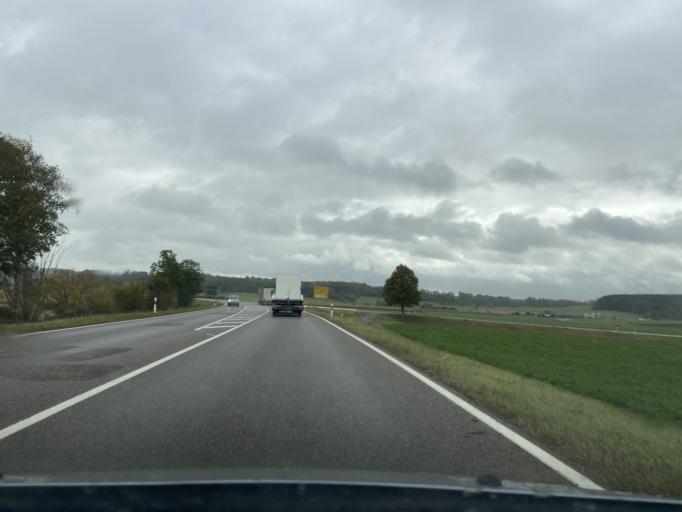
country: DE
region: Baden-Wuerttemberg
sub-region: Tuebingen Region
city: Messkirch
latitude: 48.0014
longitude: 9.1728
